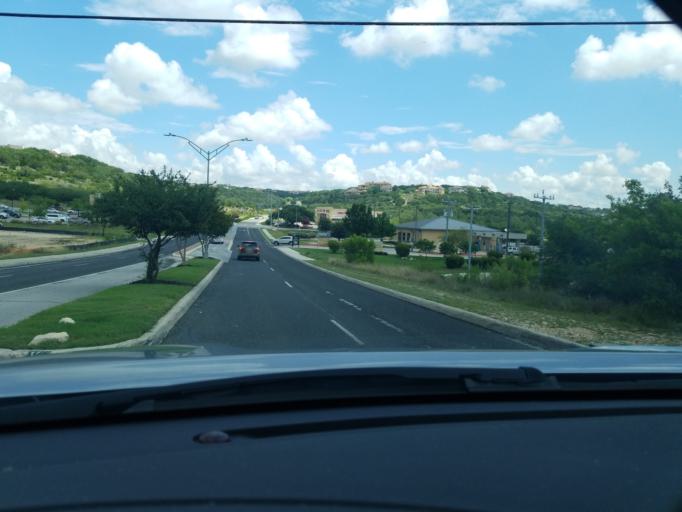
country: US
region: Texas
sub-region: Bexar County
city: Hollywood Park
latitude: 29.6414
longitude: -98.4807
